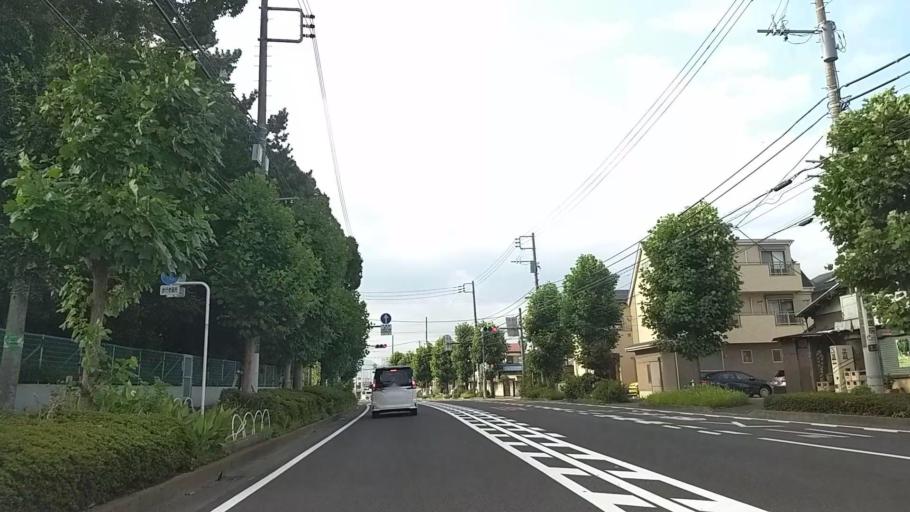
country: JP
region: Kanagawa
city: Hiratsuka
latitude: 35.3490
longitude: 139.3321
